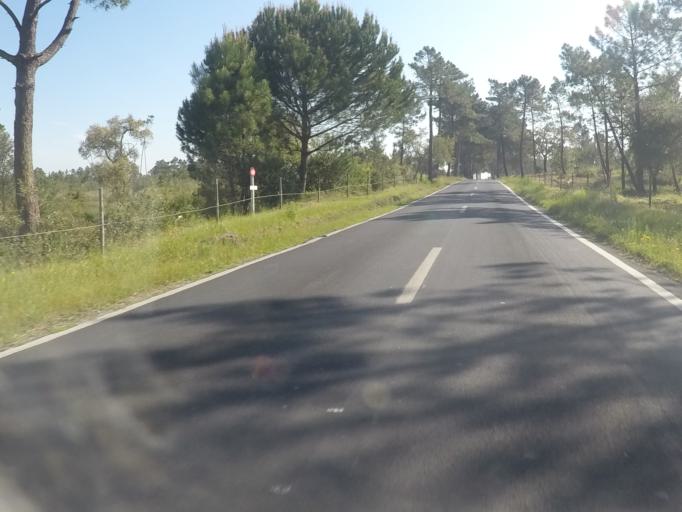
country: PT
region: Setubal
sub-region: Seixal
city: Arrentela
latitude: 38.5461
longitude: -9.1074
